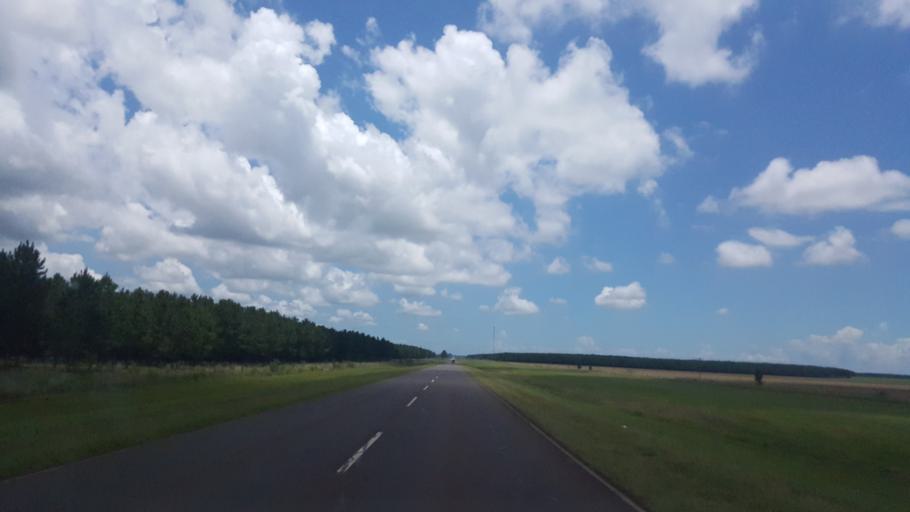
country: PY
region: Itapua
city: San Juan del Parana
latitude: -27.5127
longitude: -56.1405
